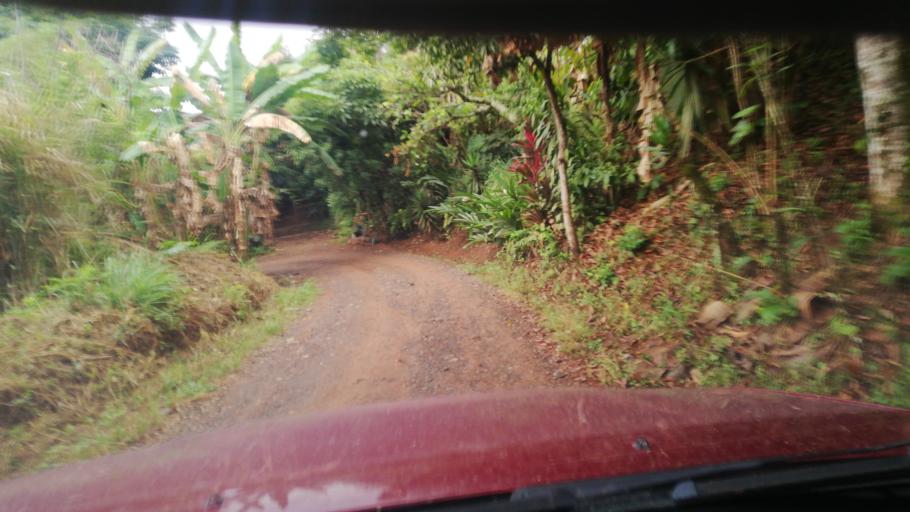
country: CO
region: Risaralda
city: La Virginia
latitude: 4.8816
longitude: -75.9487
